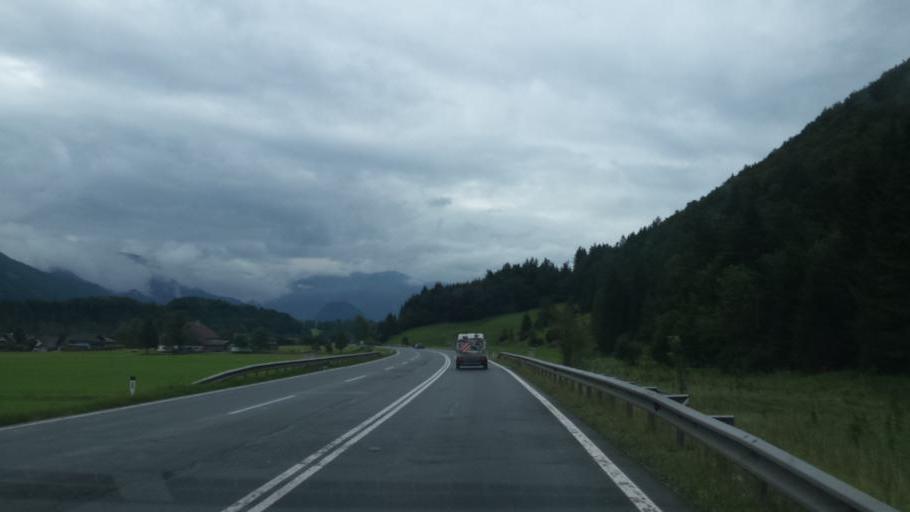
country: AT
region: Salzburg
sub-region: Politischer Bezirk Salzburg-Umgebung
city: Strobl
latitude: 47.7139
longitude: 13.5159
